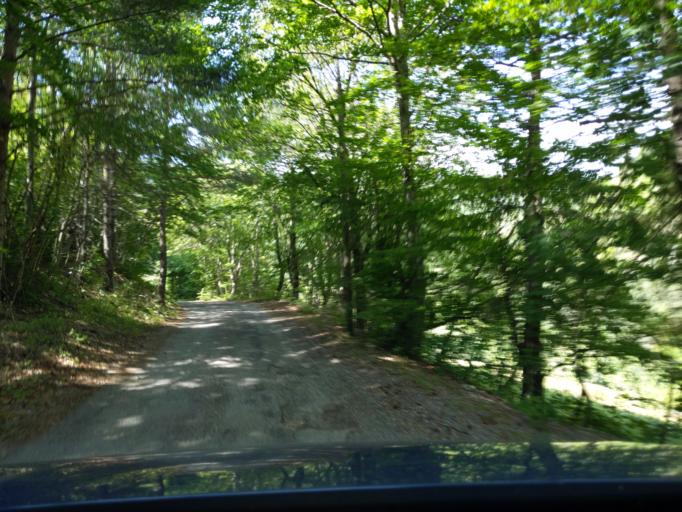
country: FR
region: Provence-Alpes-Cote d'Azur
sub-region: Departement des Hautes-Alpes
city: Veynes
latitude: 44.6330
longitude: 5.6642
